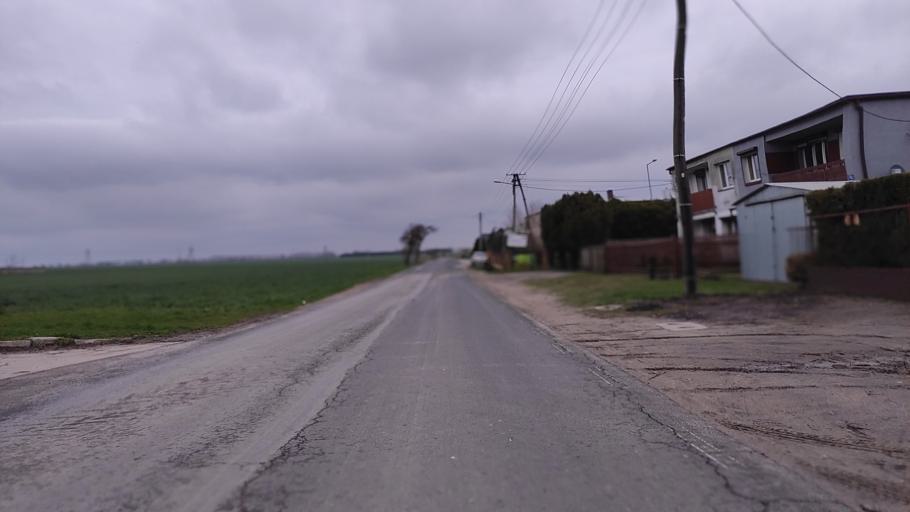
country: PL
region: Greater Poland Voivodeship
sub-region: Powiat poznanski
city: Kostrzyn
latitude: 52.4034
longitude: 17.1640
